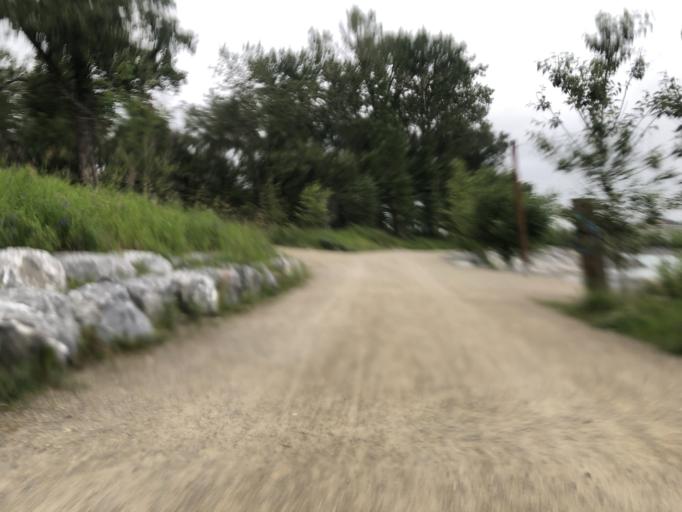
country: CA
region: Alberta
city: Calgary
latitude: 51.0415
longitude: -114.0128
